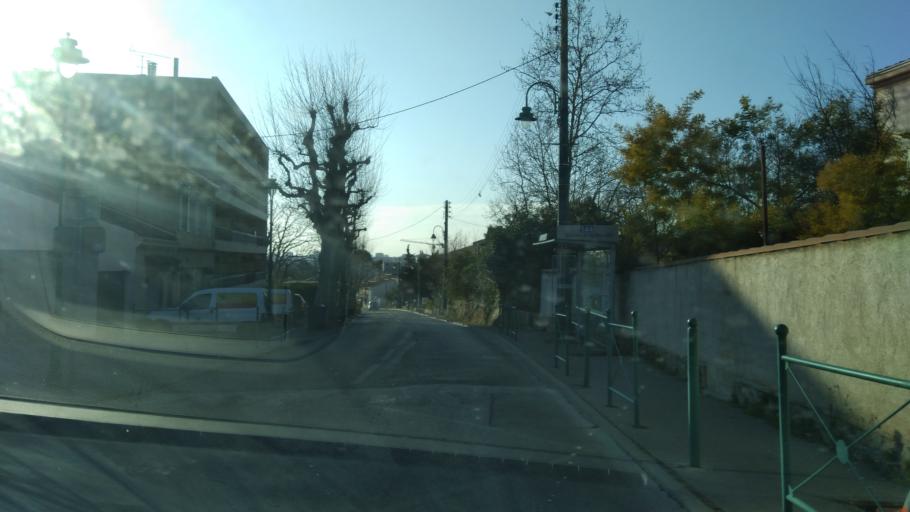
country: FR
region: Provence-Alpes-Cote d'Azur
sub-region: Departement des Bouches-du-Rhone
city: Plan-de-Cuques
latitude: 43.3329
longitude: 5.4630
